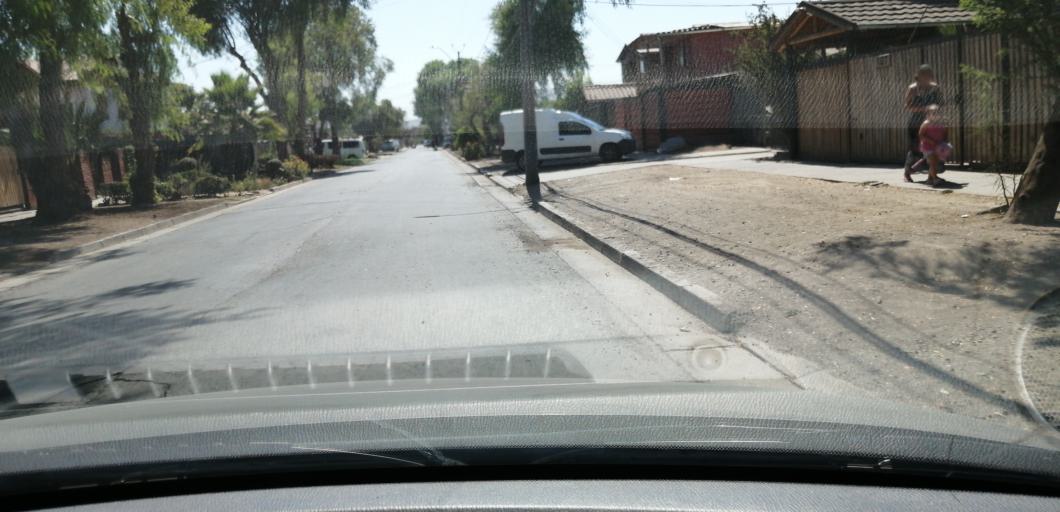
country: CL
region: Santiago Metropolitan
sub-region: Provincia de Santiago
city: Lo Prado
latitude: -33.4351
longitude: -70.7461
